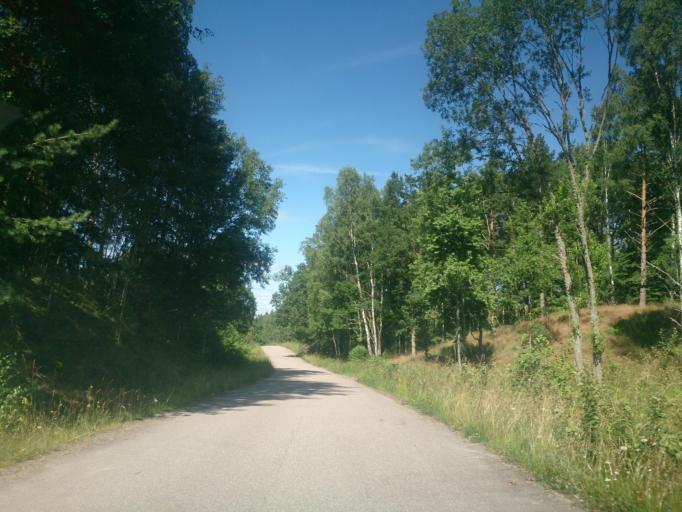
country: SE
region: OEstergoetland
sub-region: Atvidabergs Kommun
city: Atvidaberg
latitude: 58.2345
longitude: 15.9661
